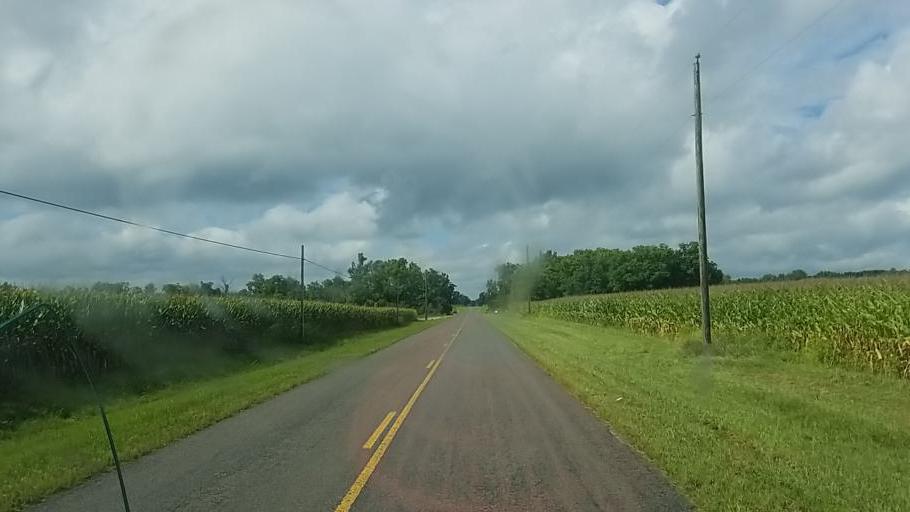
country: US
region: Ohio
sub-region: Hardin County
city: Kenton
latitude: 40.4966
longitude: -83.5190
